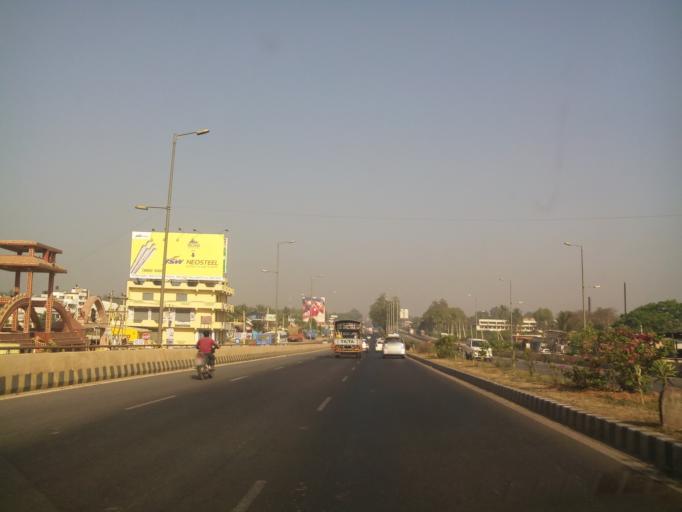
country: IN
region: Karnataka
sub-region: Bangalore Rural
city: Nelamangala
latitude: 13.0698
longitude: 77.4460
